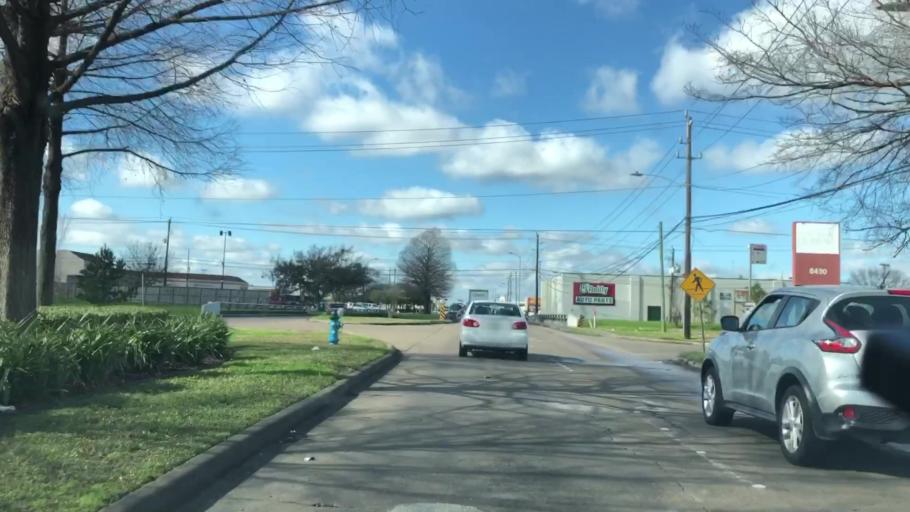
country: US
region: Texas
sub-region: Fort Bend County
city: Missouri City
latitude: 29.6561
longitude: -95.5048
